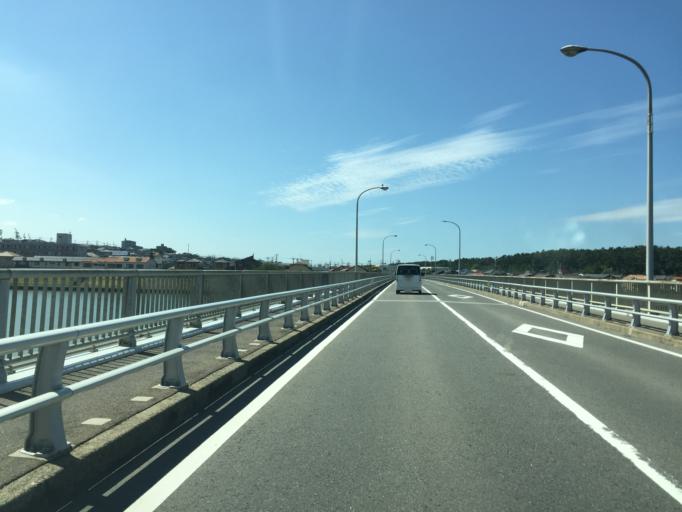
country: JP
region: Niigata
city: Niigata-shi
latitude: 37.9055
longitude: 139.0069
